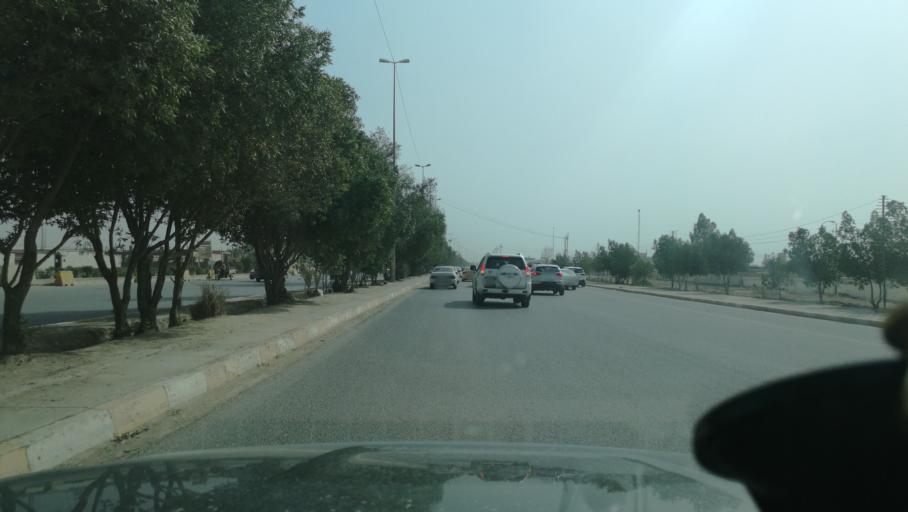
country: IQ
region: Dhi Qar
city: An Nasiriyah
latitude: 31.0750
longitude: 46.2475
